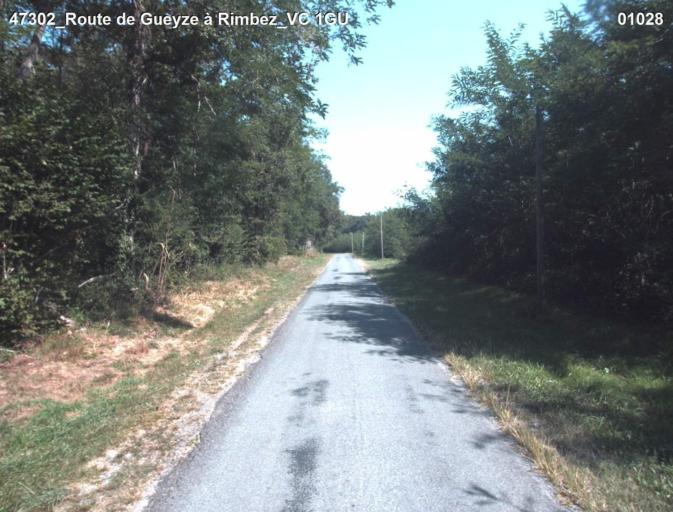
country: FR
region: Midi-Pyrenees
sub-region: Departement du Gers
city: Montreal
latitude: 44.0430
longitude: 0.1239
